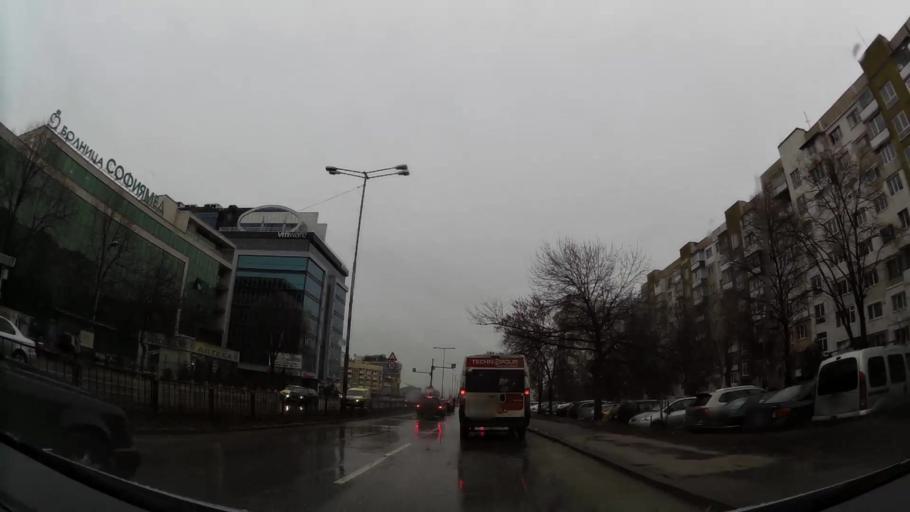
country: BG
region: Sofia-Capital
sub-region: Stolichna Obshtina
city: Sofia
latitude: 42.6665
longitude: 23.3644
